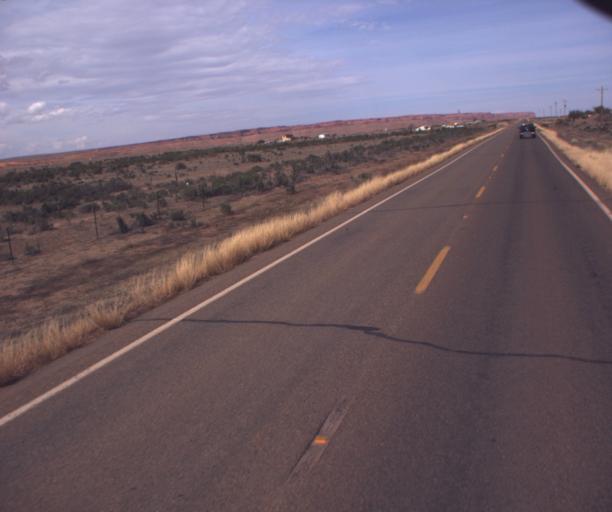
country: US
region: Arizona
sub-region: Apache County
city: Many Farms
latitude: 36.4305
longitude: -109.6067
